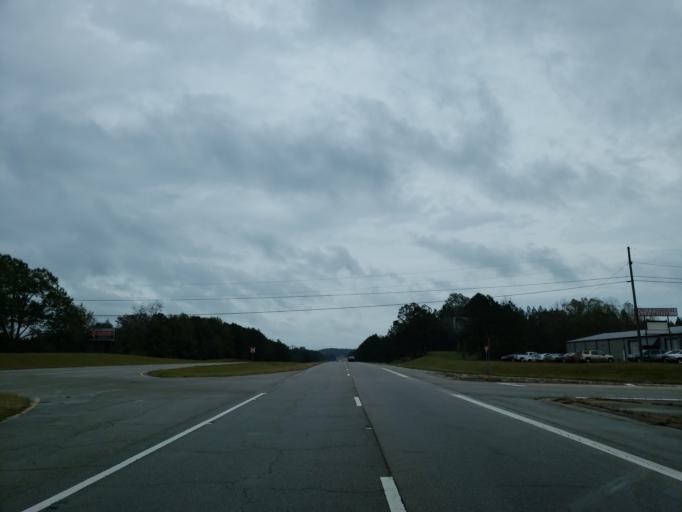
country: US
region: Mississippi
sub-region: Jones County
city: Laurel
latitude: 31.7015
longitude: -89.0903
